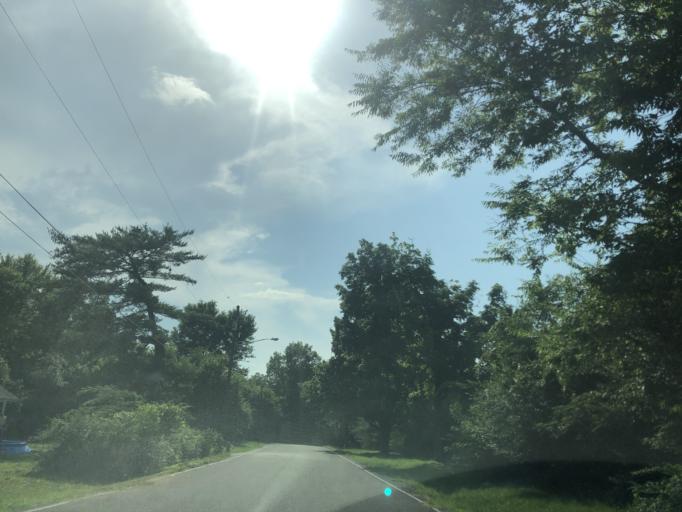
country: US
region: Tennessee
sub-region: Davidson County
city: Oak Hill
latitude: 36.1073
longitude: -86.6911
